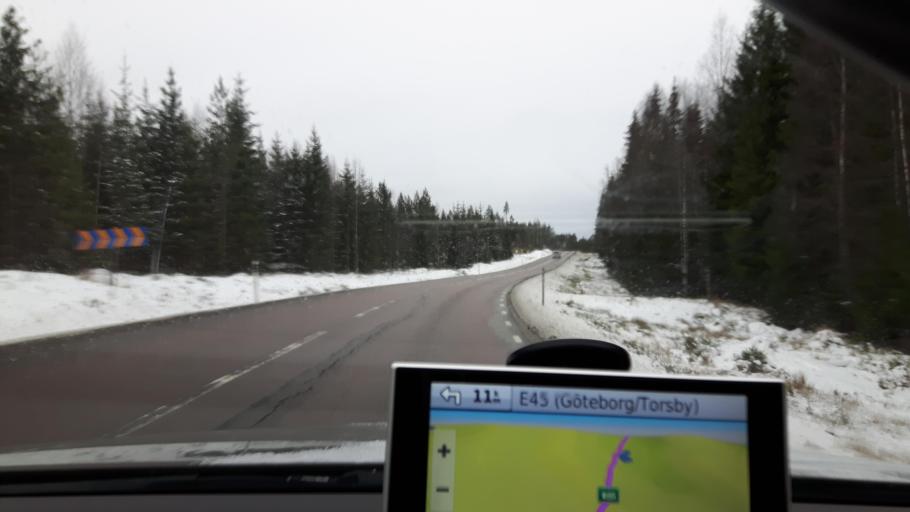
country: SE
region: Vaermland
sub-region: Torsby Kommun
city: Torsby
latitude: 60.3492
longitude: 13.1677
